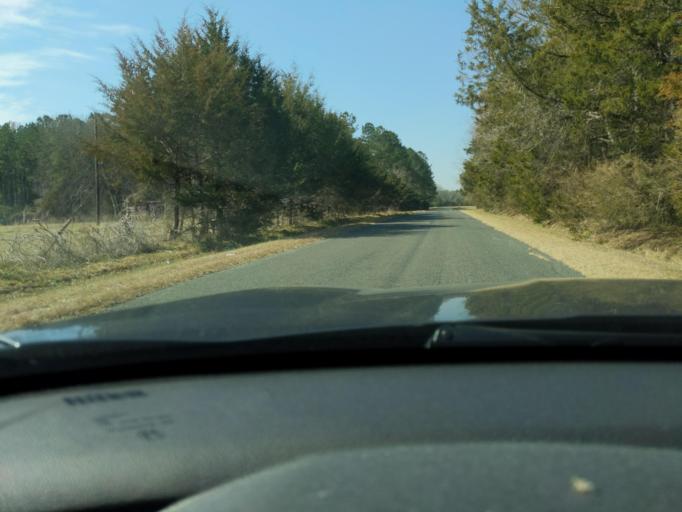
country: US
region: South Carolina
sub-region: Abbeville County
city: Calhoun Falls
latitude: 34.0862
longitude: -82.5539
